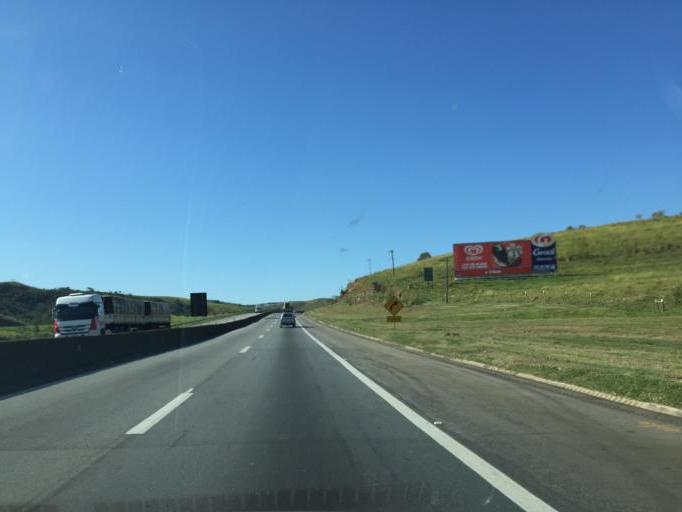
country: BR
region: Sao Paulo
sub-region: Cruzeiro
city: Cruzeiro
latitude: -22.6640
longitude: -44.9829
